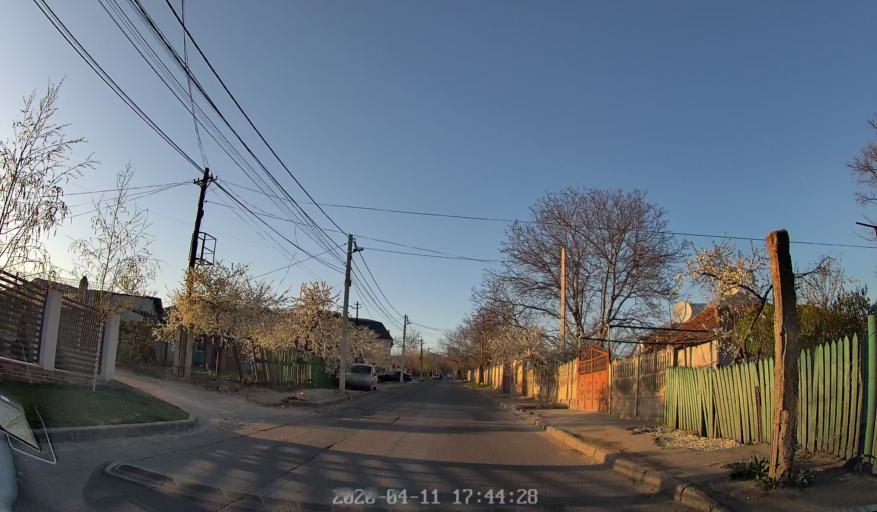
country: MD
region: Chisinau
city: Chisinau
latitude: 46.9781
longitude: 28.8239
